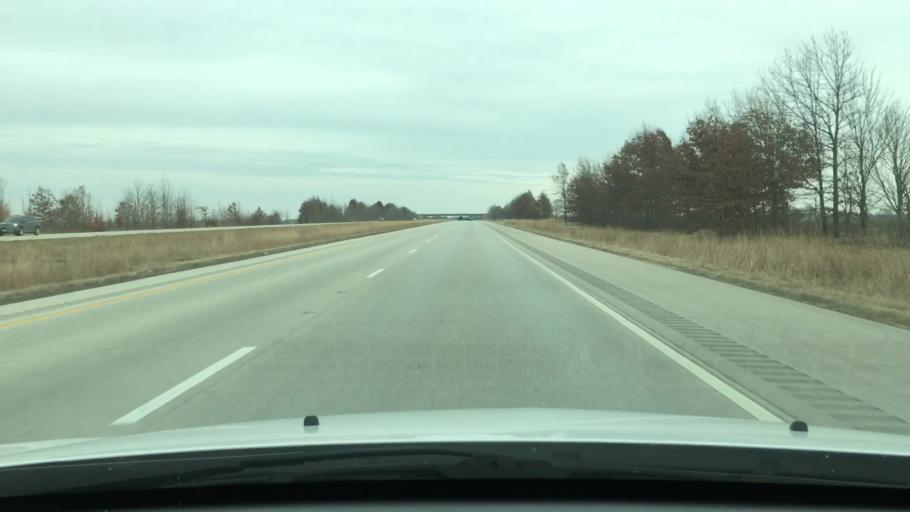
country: US
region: Illinois
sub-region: Sangamon County
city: New Berlin
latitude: 39.7408
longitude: -89.8553
